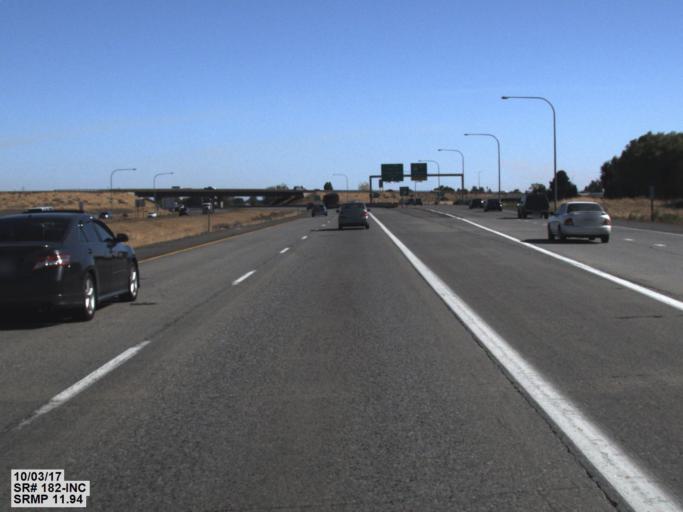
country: US
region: Washington
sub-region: Franklin County
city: Pasco
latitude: 46.2501
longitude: -119.1325
